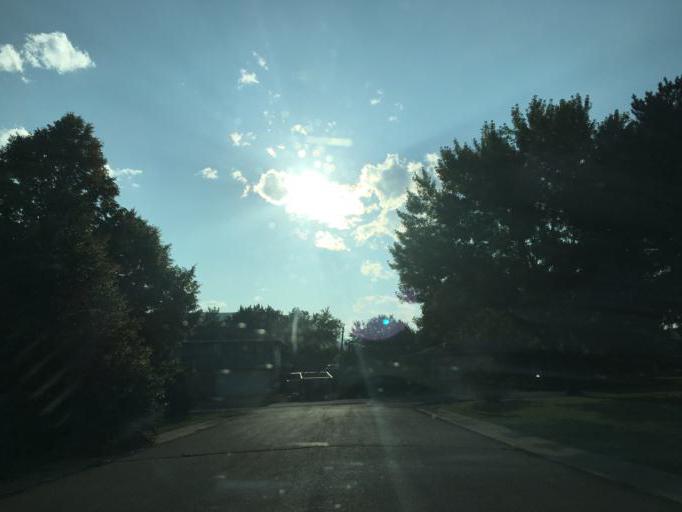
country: US
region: Colorado
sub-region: Jefferson County
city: Applewood
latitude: 39.7940
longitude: -105.1700
